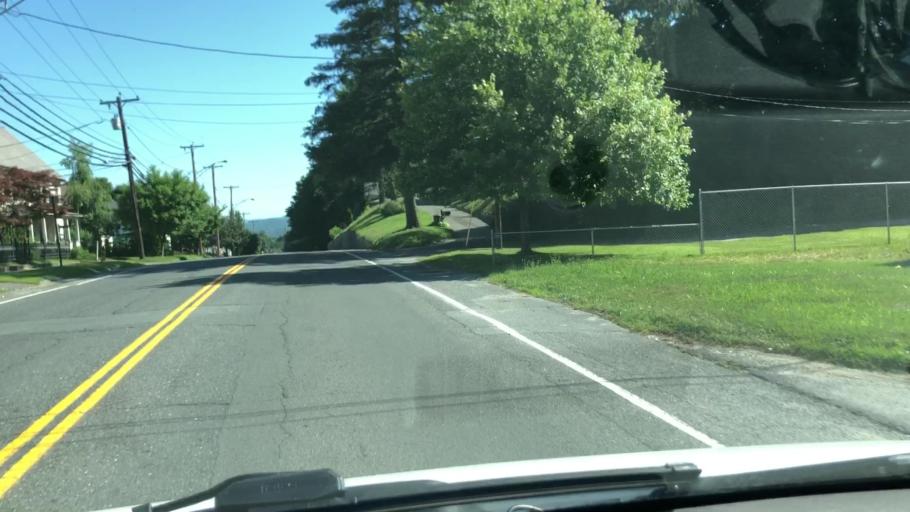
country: US
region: Massachusetts
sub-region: Berkshire County
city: Adams
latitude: 42.6114
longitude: -73.1255
